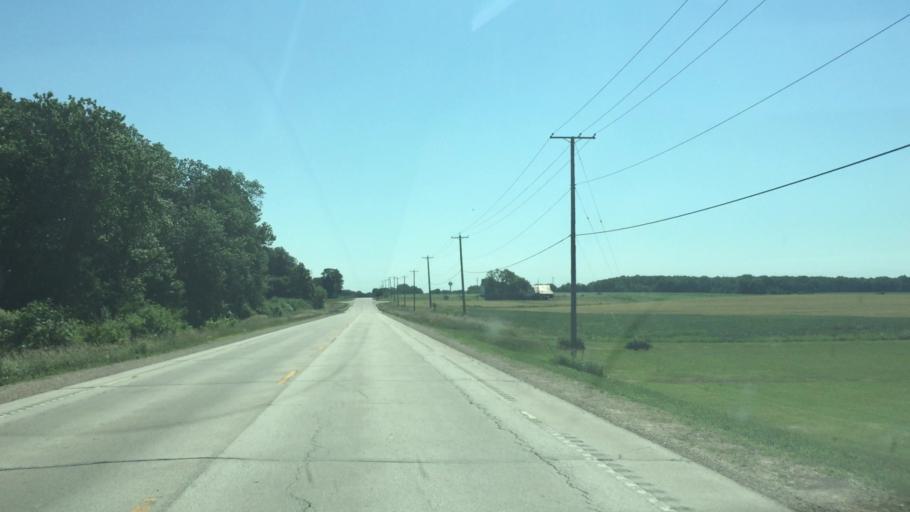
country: US
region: Wisconsin
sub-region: Calumet County
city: Hilbert
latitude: 44.1402
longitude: -88.1900
